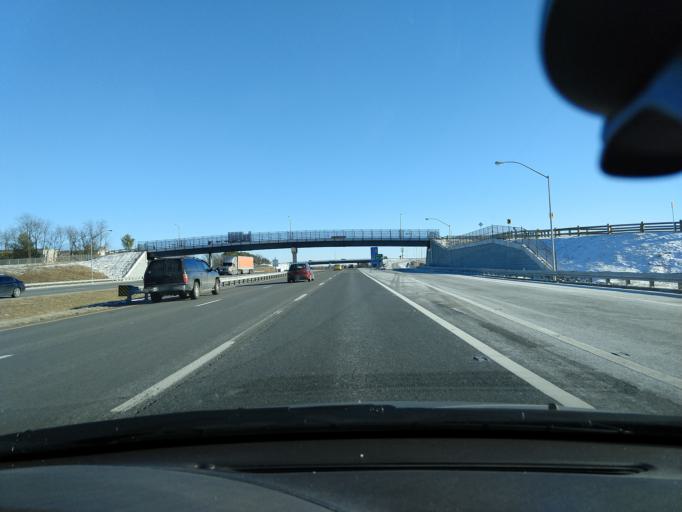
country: US
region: Virginia
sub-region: City of Roanoke
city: Roanoke
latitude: 37.2996
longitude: -79.9621
